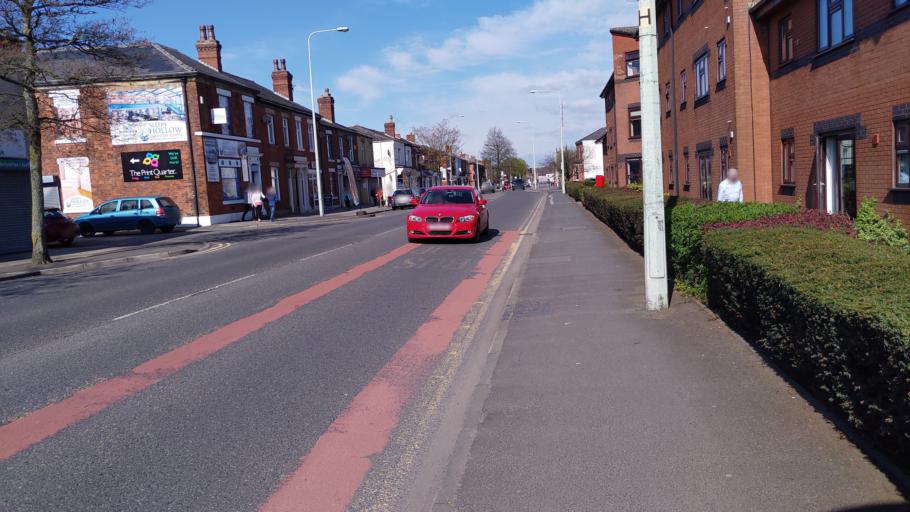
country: GB
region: England
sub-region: Lancashire
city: Chorley
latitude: 53.6464
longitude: -2.6349
